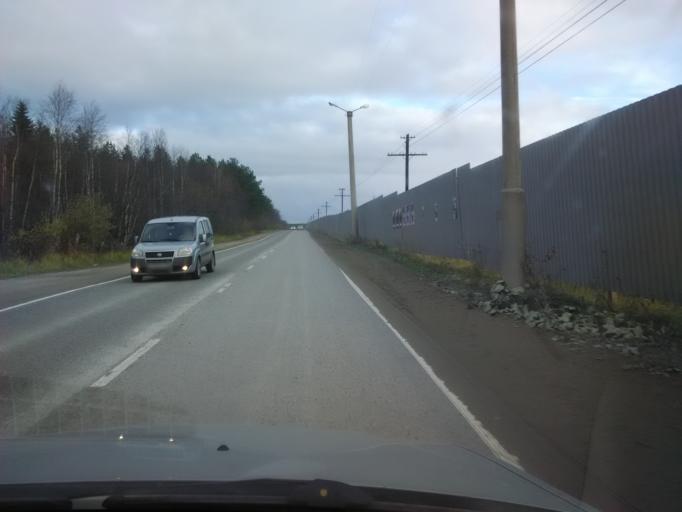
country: RU
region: Murmansk
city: Polyarnyye Zori
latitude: 67.3814
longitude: 32.5099
